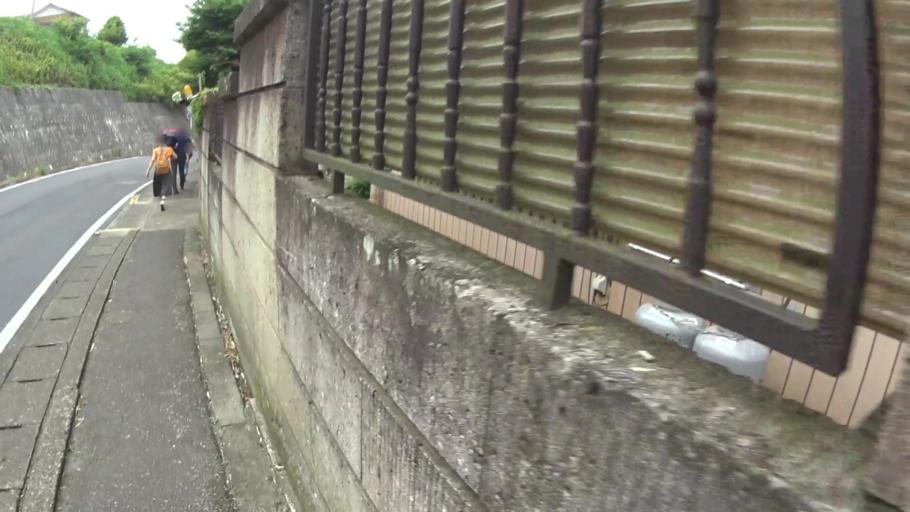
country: JP
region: Chiba
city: Sawara
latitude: 35.8853
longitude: 140.4905
